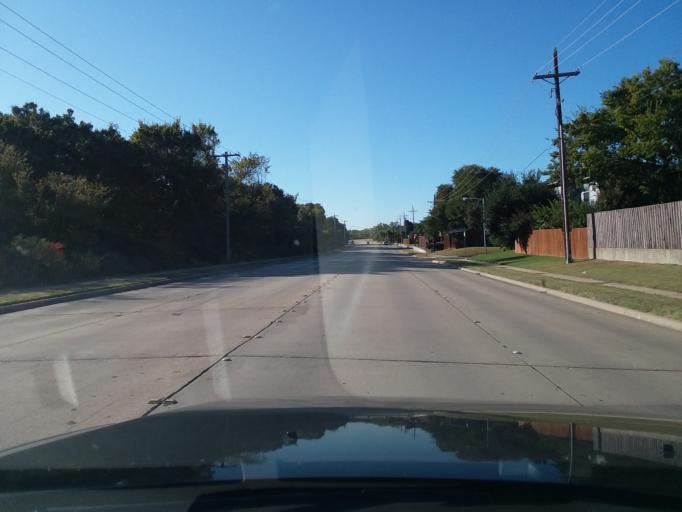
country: US
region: Texas
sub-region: Denton County
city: Lewisville
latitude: 33.0239
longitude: -97.0279
